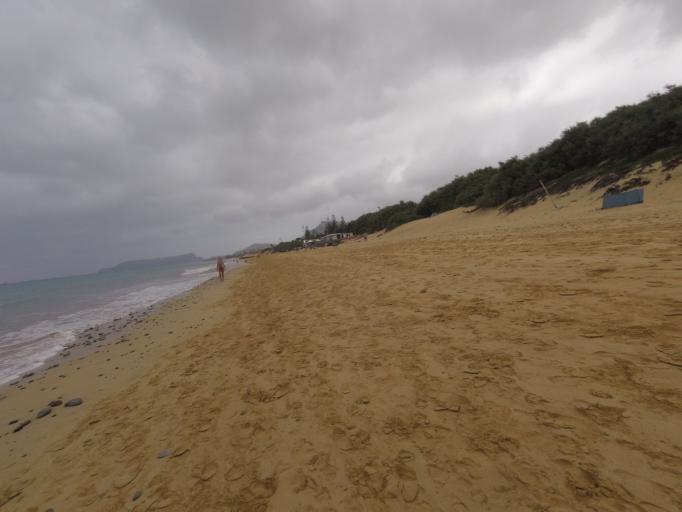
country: PT
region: Madeira
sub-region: Porto Santo
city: Vila de Porto Santo
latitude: 33.0567
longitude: -16.3361
